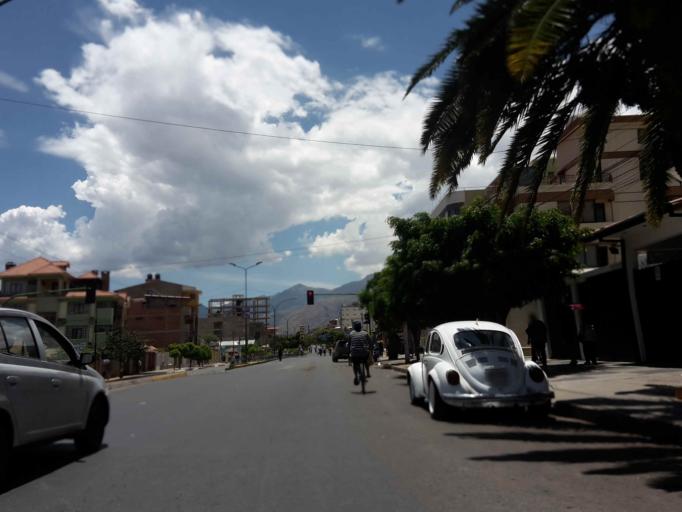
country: BO
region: Cochabamba
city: Cochabamba
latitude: -17.3537
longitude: -66.1885
